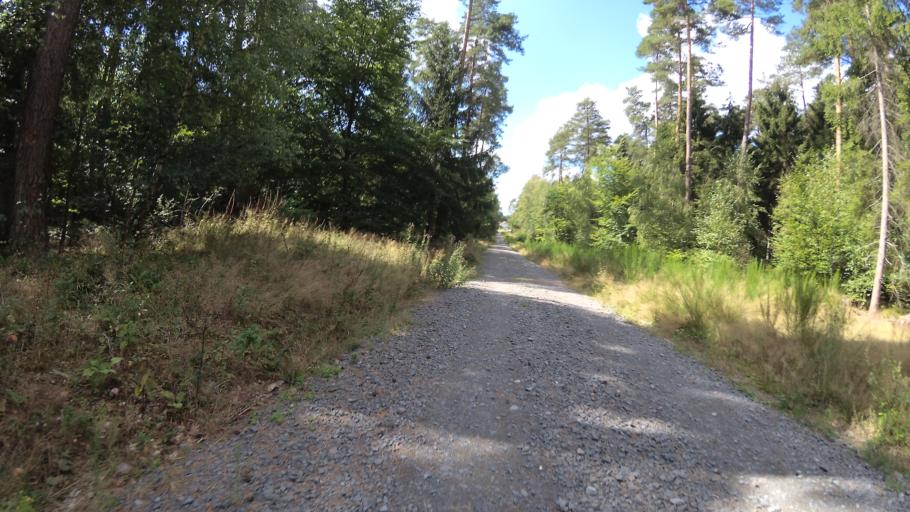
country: DE
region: Saarland
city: Homburg
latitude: 49.3273
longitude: 7.2996
